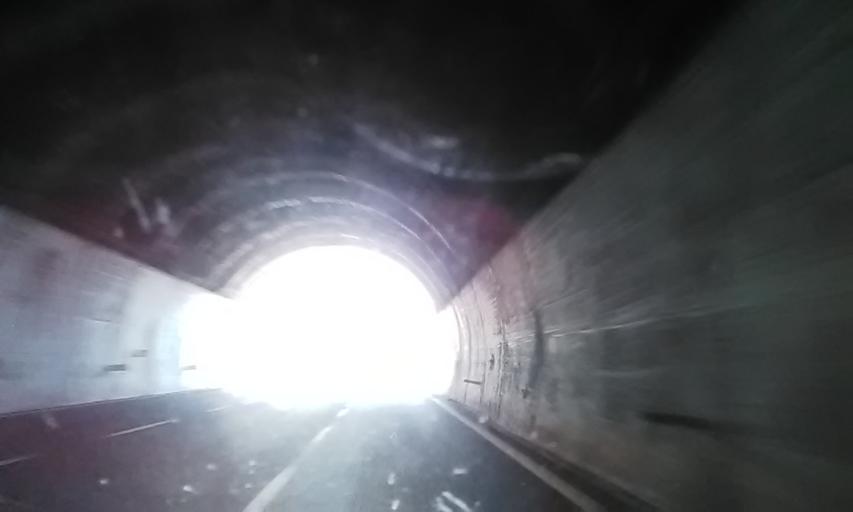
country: IT
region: Liguria
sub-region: Provincia di Savona
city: Celle Ligure
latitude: 44.3456
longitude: 8.5414
